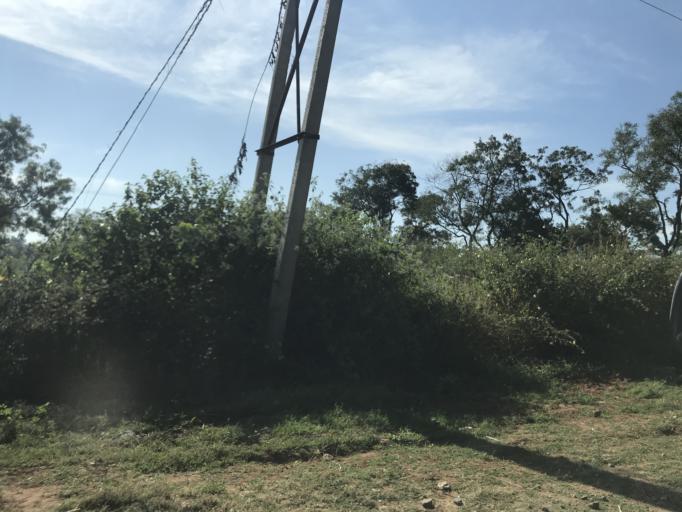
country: IN
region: Karnataka
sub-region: Mysore
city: Mysore
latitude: 12.1934
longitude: 76.5431
